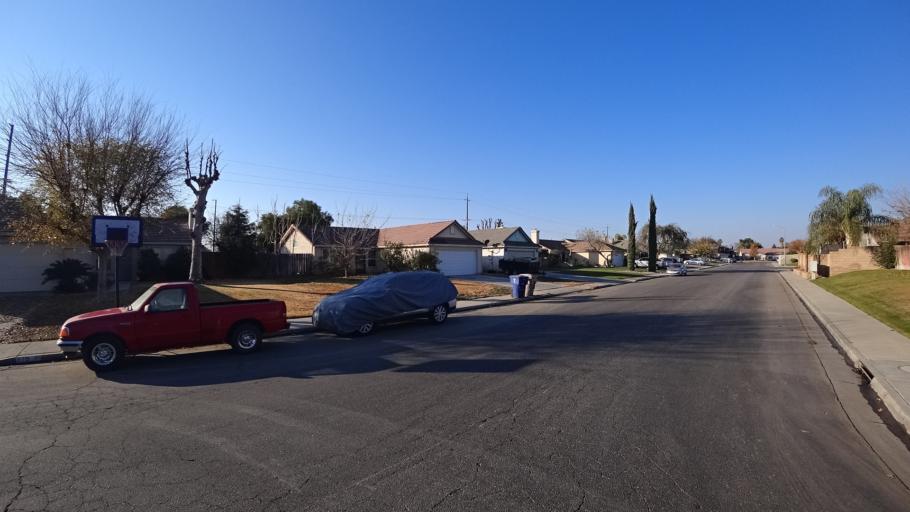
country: US
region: California
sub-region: Kern County
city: Greenfield
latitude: 35.2964
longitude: -119.0091
